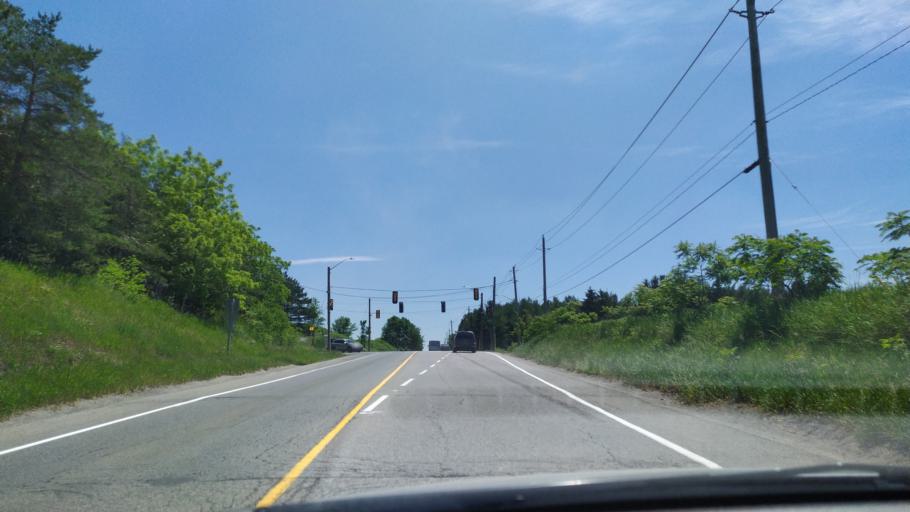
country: CA
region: Ontario
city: Kitchener
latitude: 43.3975
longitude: -80.5355
